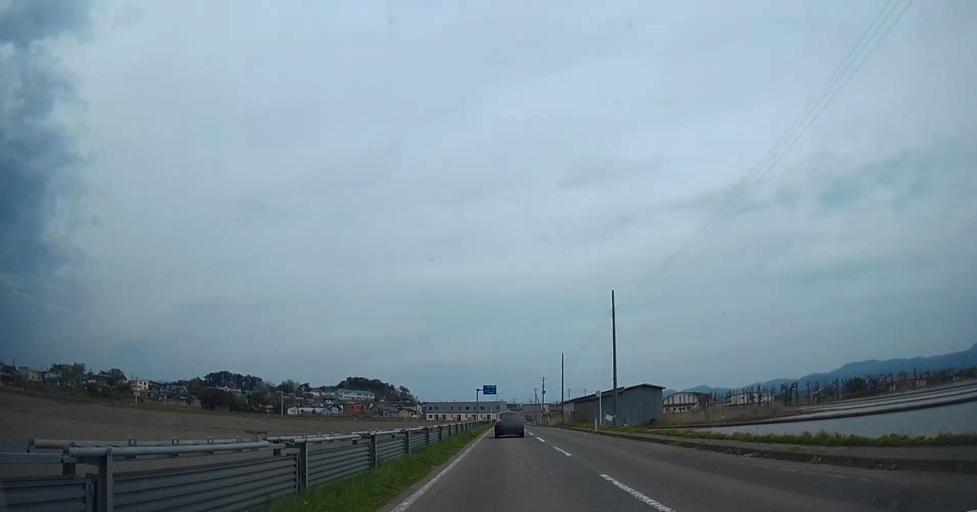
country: JP
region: Aomori
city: Shimokizukuri
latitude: 40.9758
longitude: 140.3693
